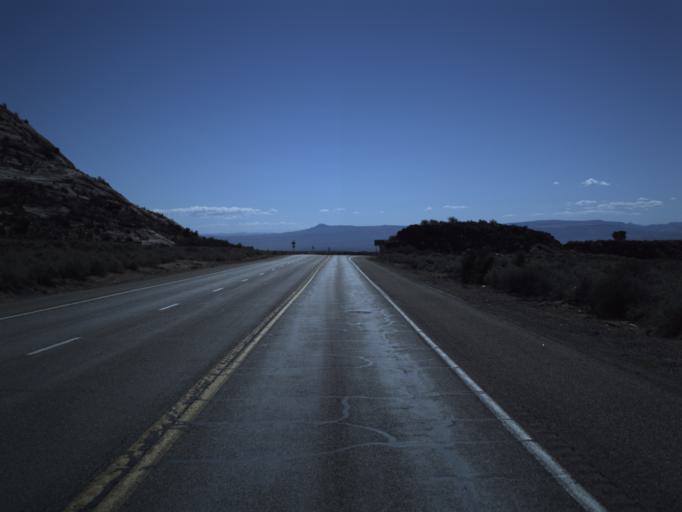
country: US
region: Utah
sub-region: Washington County
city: Ivins
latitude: 37.2339
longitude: -113.6347
